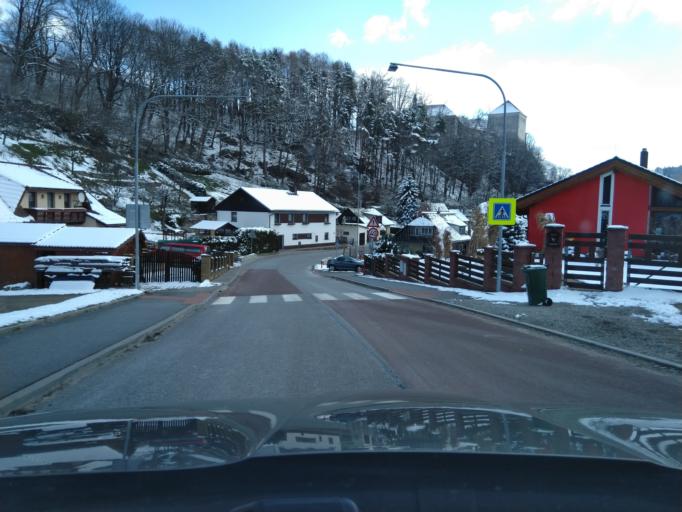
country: CZ
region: Jihocesky
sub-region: Okres Prachatice
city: Vimperk
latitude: 49.0553
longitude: 13.7683
